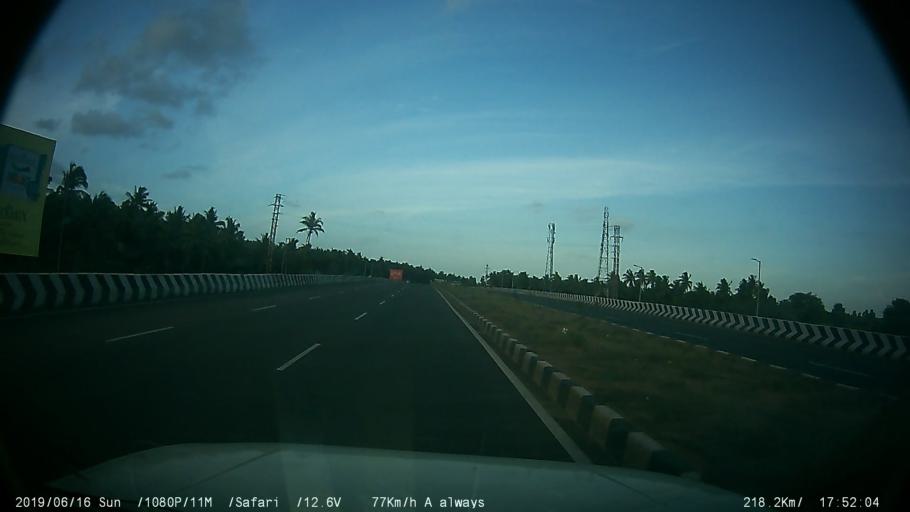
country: IN
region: Tamil Nadu
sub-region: Coimbatore
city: Madukkarai
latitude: 10.8549
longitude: 76.8466
